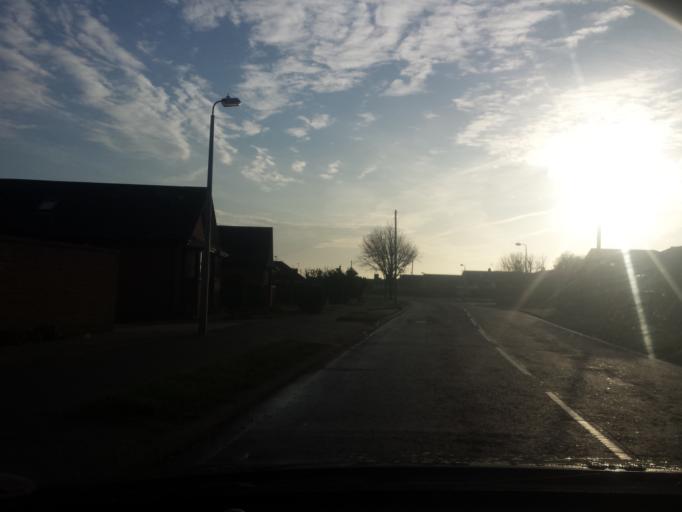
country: GB
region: England
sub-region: Essex
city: Little Clacton
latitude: 51.8170
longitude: 1.1629
